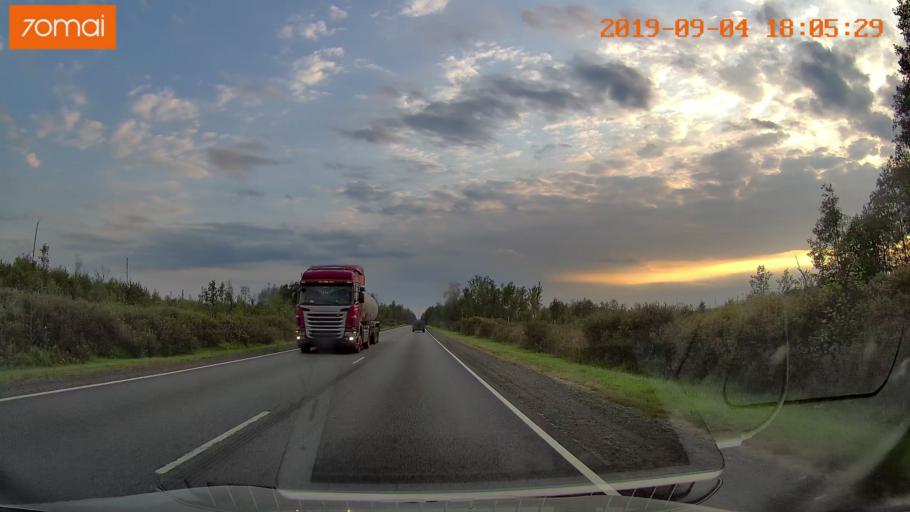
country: RU
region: Moskovskaya
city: Il'inskiy Pogost
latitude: 55.4409
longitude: 38.8260
